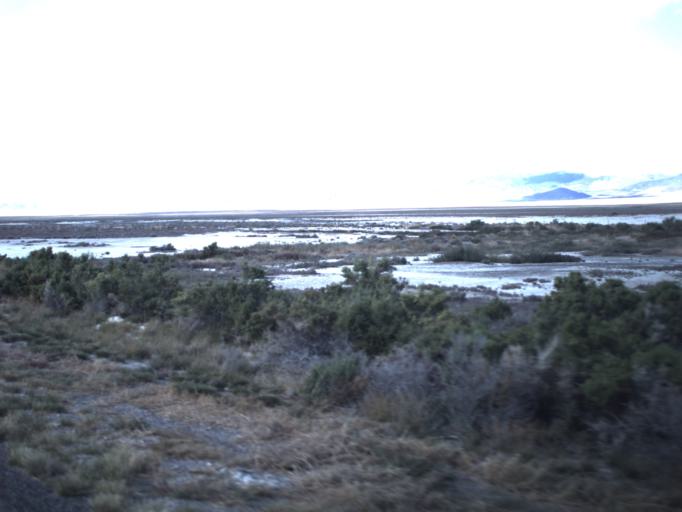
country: US
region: Utah
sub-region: Millard County
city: Delta
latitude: 39.0313
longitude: -112.7751
